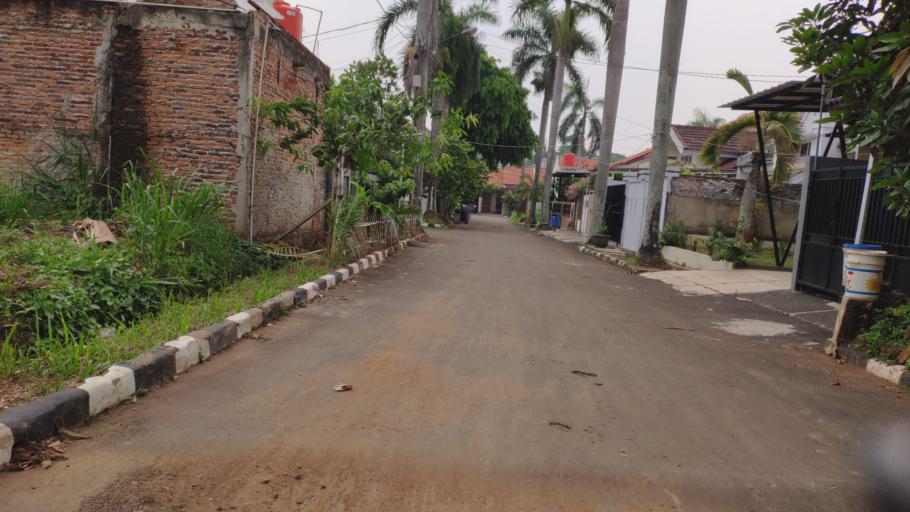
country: ID
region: West Java
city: Depok
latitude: -6.3775
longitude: 106.7978
